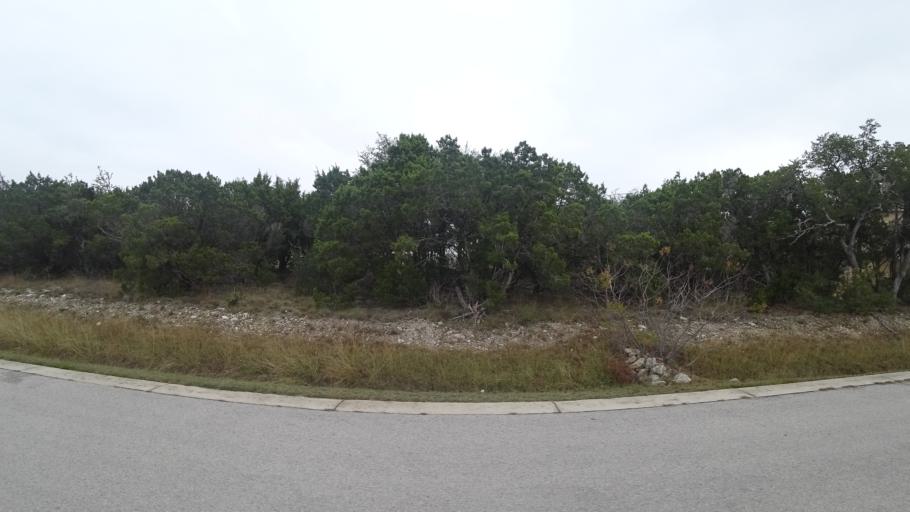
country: US
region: Texas
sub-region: Travis County
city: Hudson Bend
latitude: 30.3874
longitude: -97.9193
